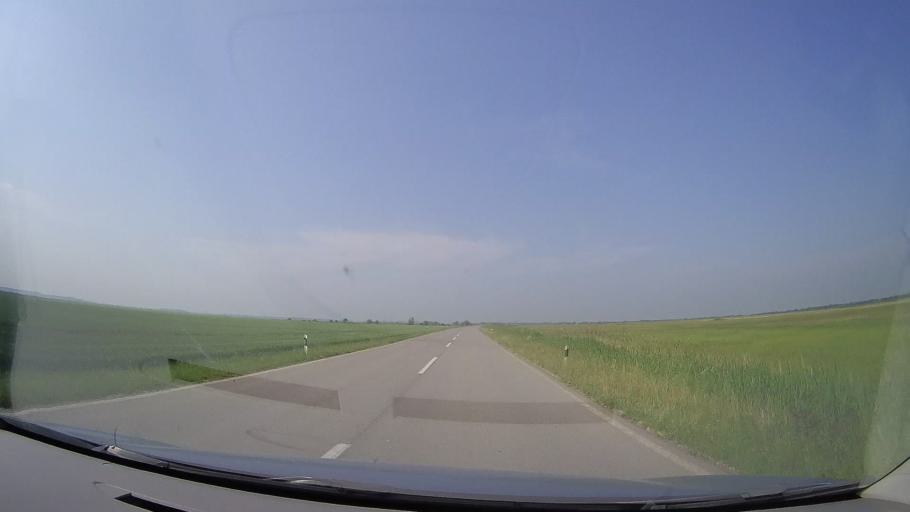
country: RS
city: Jasa Tomic
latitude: 45.4115
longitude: 20.8281
